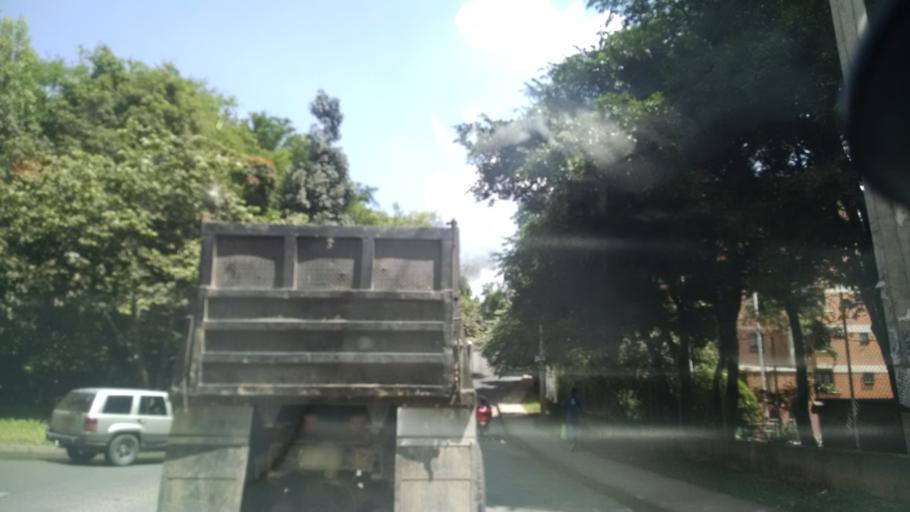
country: CO
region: Antioquia
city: Itagui
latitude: 6.2161
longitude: -75.5998
